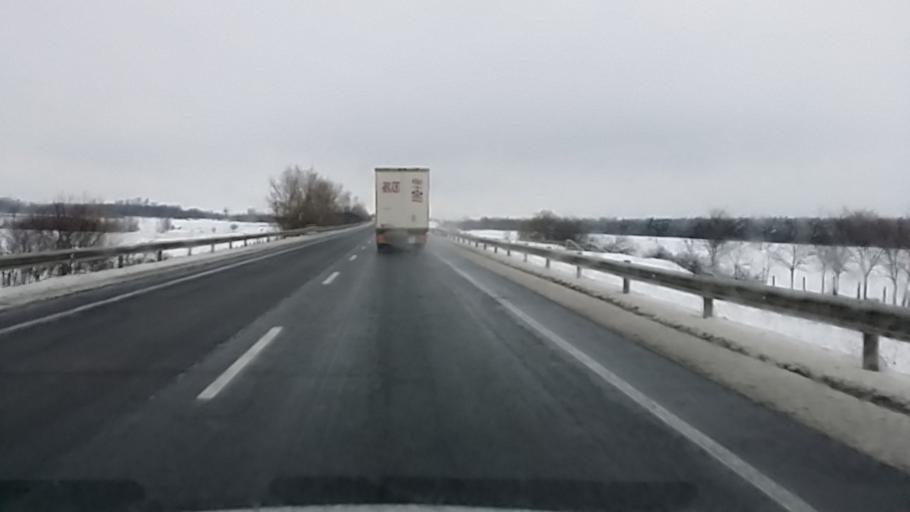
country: HU
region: Gyor-Moson-Sopron
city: Rajka
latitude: 47.9281
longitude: 17.1722
